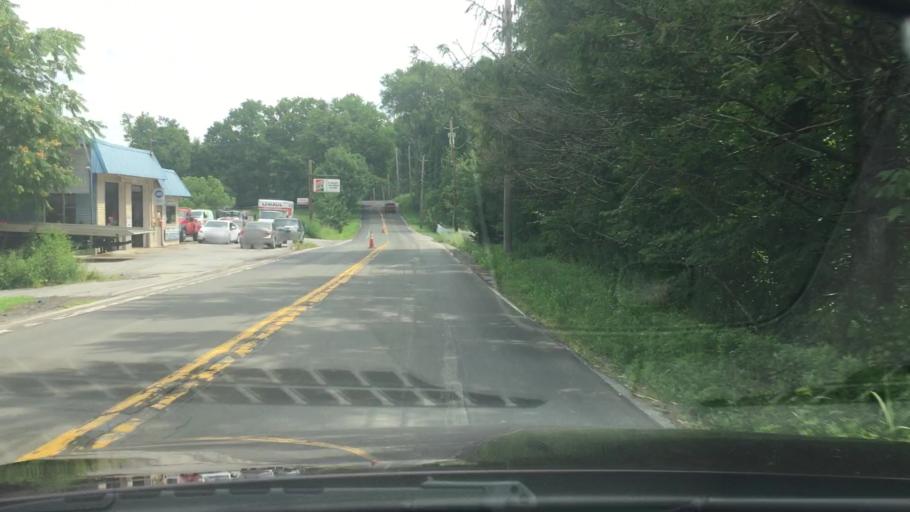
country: US
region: New York
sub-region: Dutchess County
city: Hillside Lake
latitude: 41.5876
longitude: -73.7089
